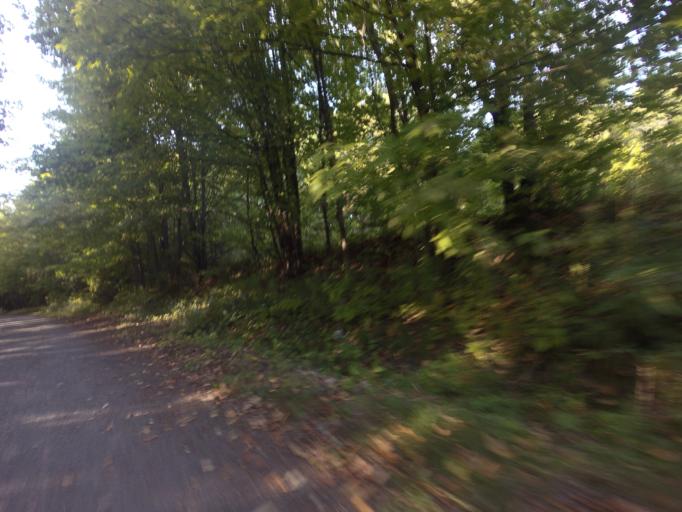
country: CA
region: Quebec
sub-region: Laurentides
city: Saint-Jerome
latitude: 45.8116
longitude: -74.0221
